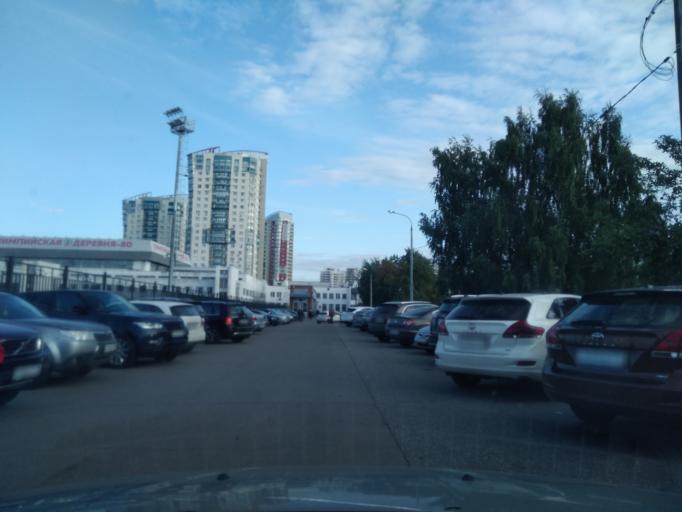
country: RU
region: Moscow
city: Nikulino
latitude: 55.6769
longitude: 37.4718
